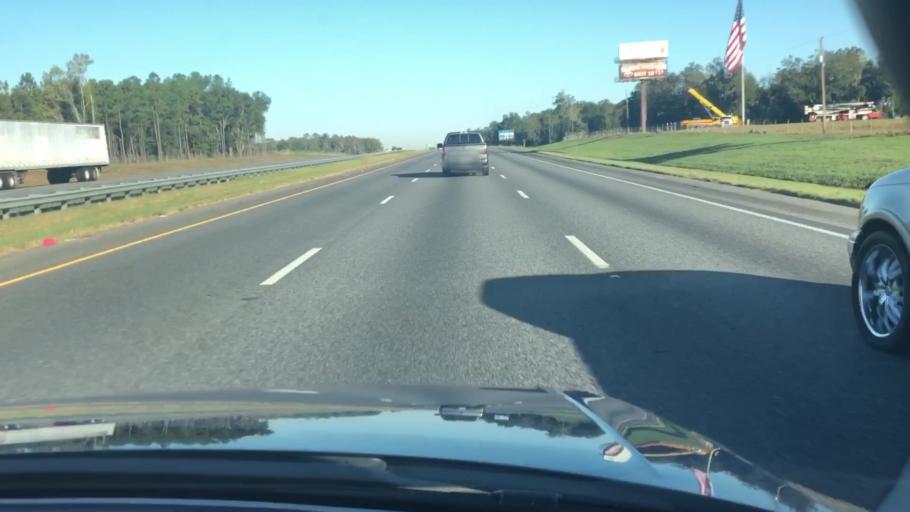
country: US
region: Georgia
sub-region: Lowndes County
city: Valdosta
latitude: 30.7989
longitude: -83.3057
